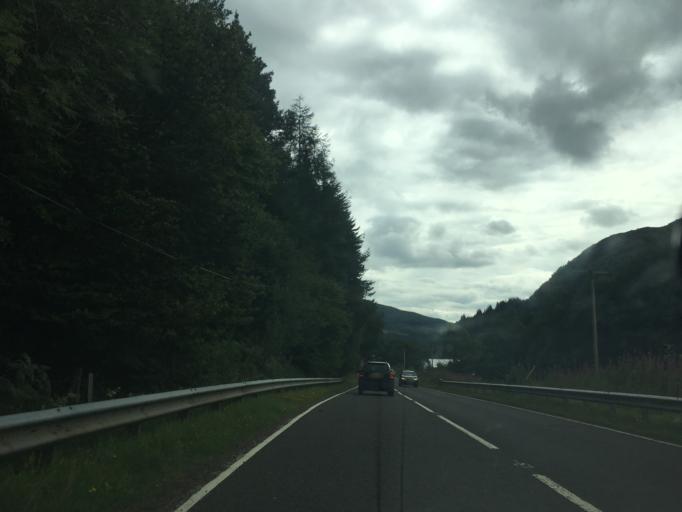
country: GB
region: Scotland
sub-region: Stirling
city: Callander
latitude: 56.2985
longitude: -4.3047
